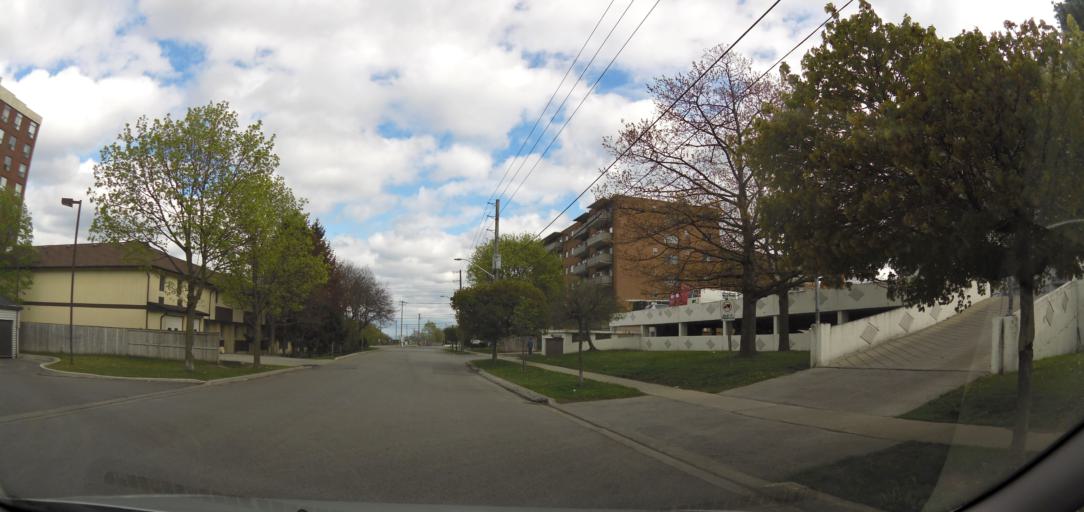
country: CA
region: Ontario
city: Etobicoke
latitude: 43.5837
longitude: -79.5538
